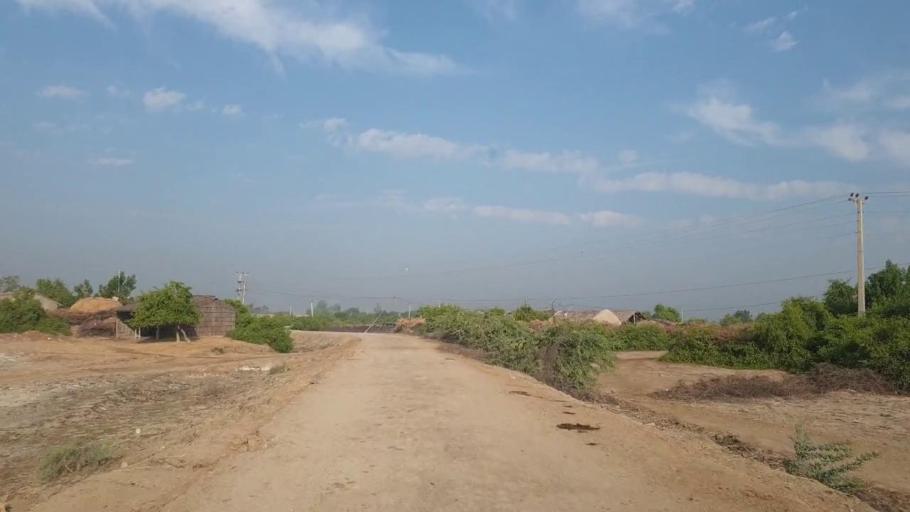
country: PK
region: Sindh
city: Tando Bago
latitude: 24.8211
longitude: 68.9759
